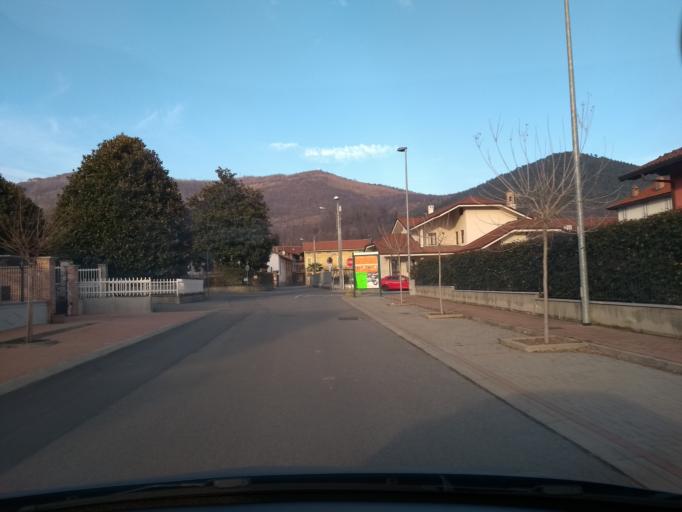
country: IT
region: Piedmont
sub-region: Provincia di Torino
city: Balangero
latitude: 45.2735
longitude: 7.5180
